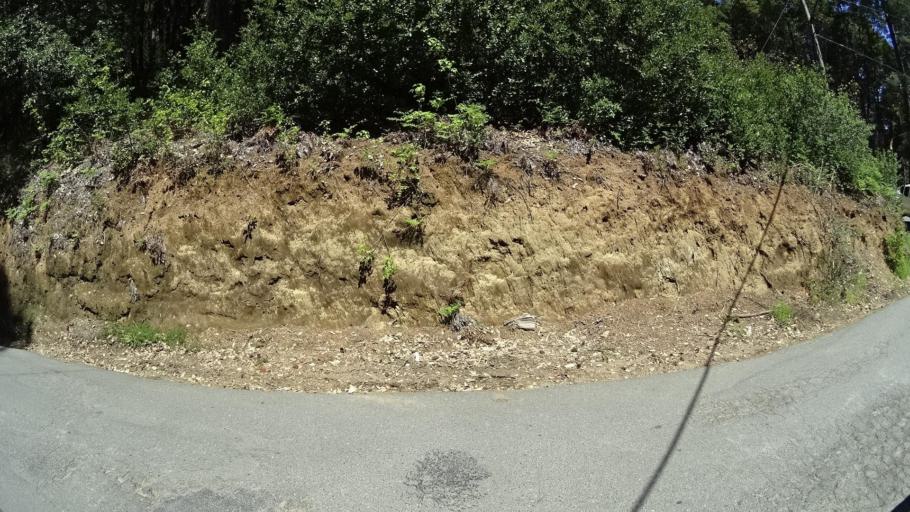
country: US
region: California
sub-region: Humboldt County
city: Redway
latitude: 40.0887
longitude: -123.9447
